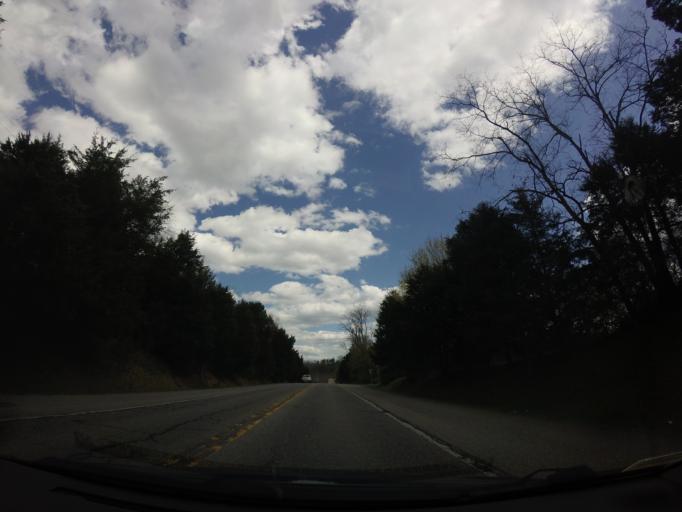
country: US
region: Maryland
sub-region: Washington County
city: Keedysville
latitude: 39.4634
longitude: -77.7311
